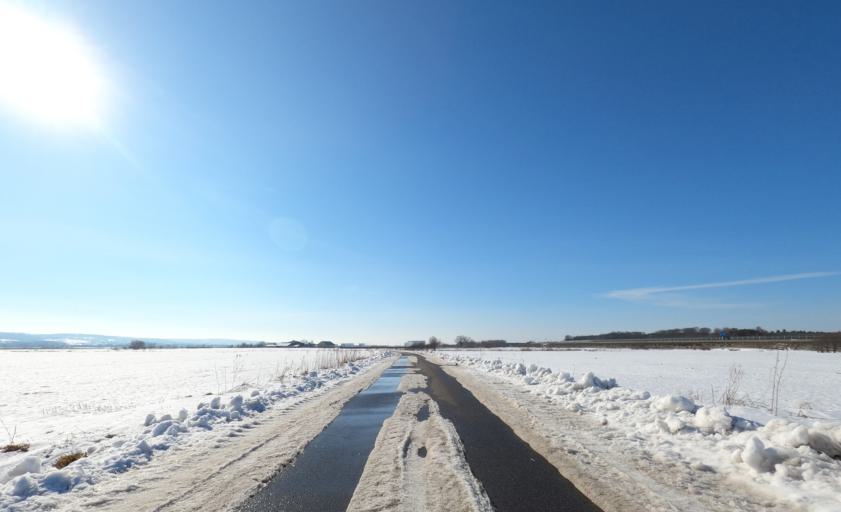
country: PL
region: Subcarpathian Voivodeship
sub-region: Powiat debicki
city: Brzeznica
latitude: 50.0819
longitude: 21.4934
